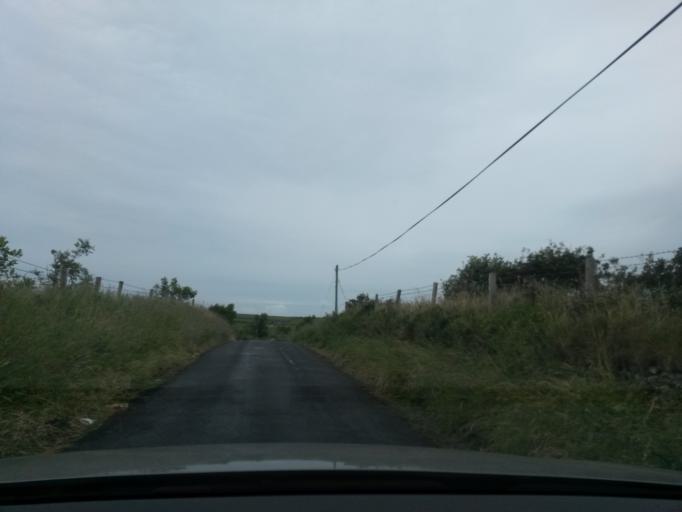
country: IE
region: Connaught
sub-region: Sligo
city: Strandhill
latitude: 54.2667
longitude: -8.7621
